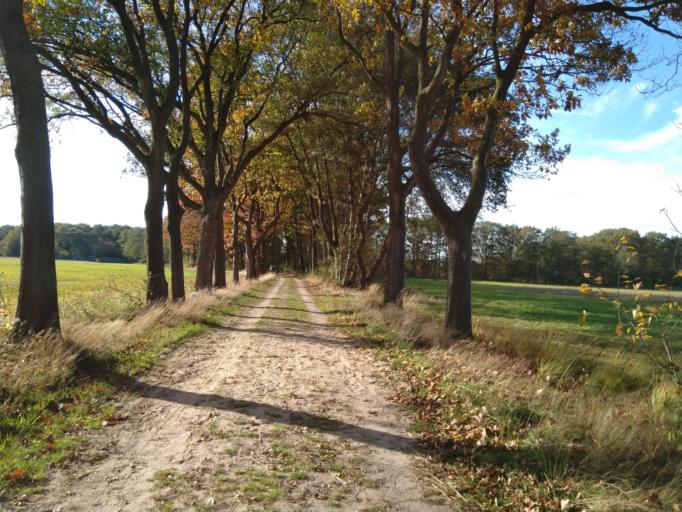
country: NL
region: Drenthe
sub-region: Gemeente Tynaarlo
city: Tynaarlo
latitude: 53.0500
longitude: 6.6539
